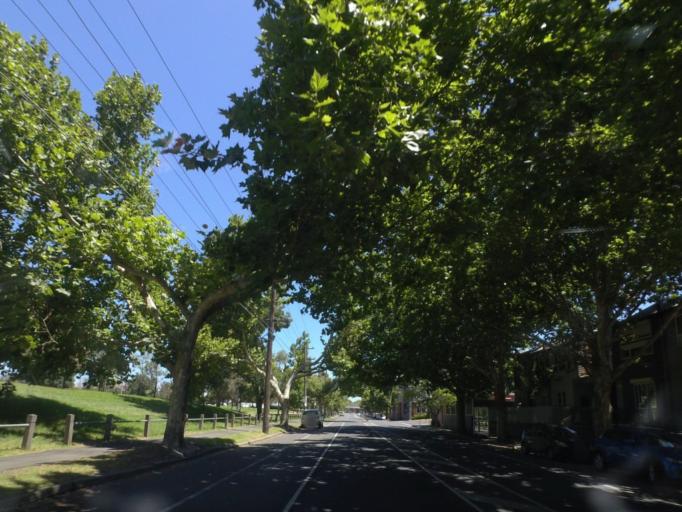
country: AU
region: Victoria
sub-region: Moonee Valley
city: Flemington
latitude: -37.7970
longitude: 144.9229
